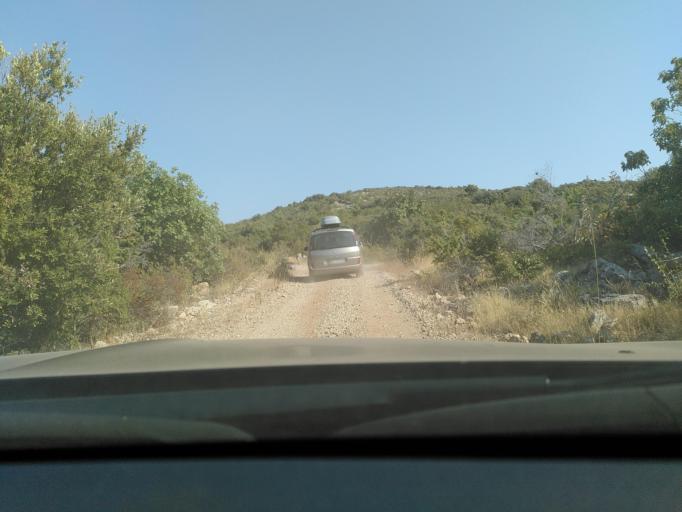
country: HR
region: Splitsko-Dalmatinska
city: Stari Grad
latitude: 43.1604
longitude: 16.5570
